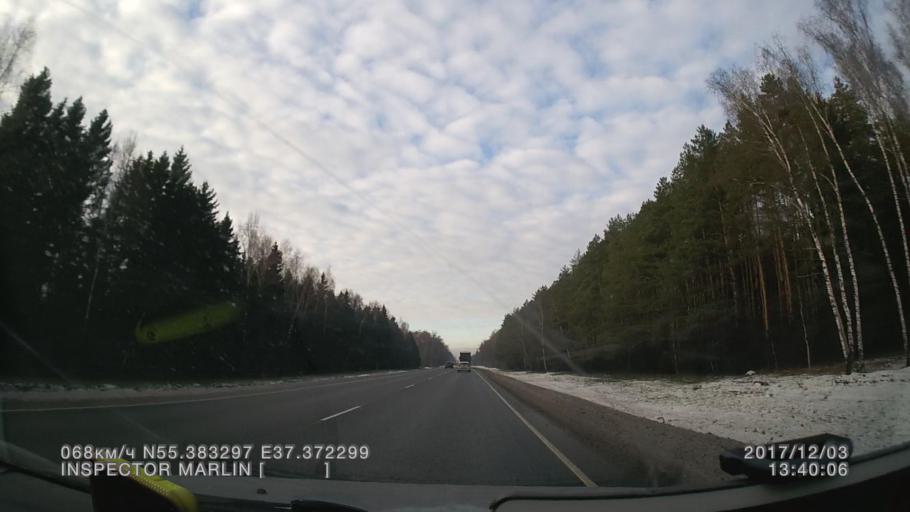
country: RU
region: Moskovskaya
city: Troitsk
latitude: 55.3833
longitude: 37.3722
